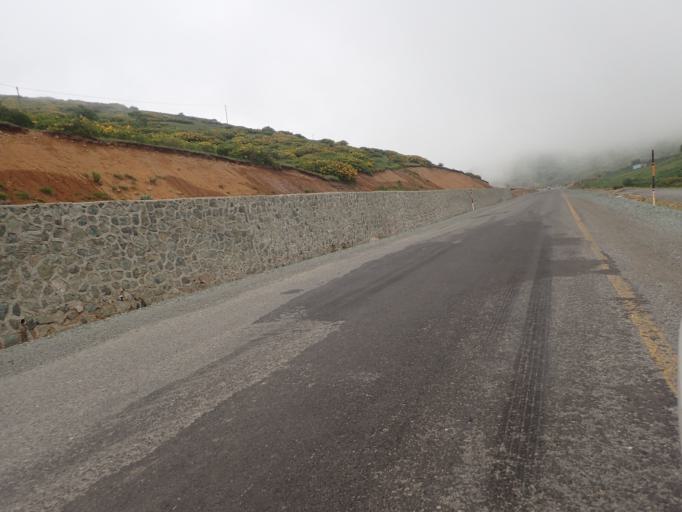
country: TR
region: Ordu
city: Topcam
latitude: 40.6659
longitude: 37.9346
